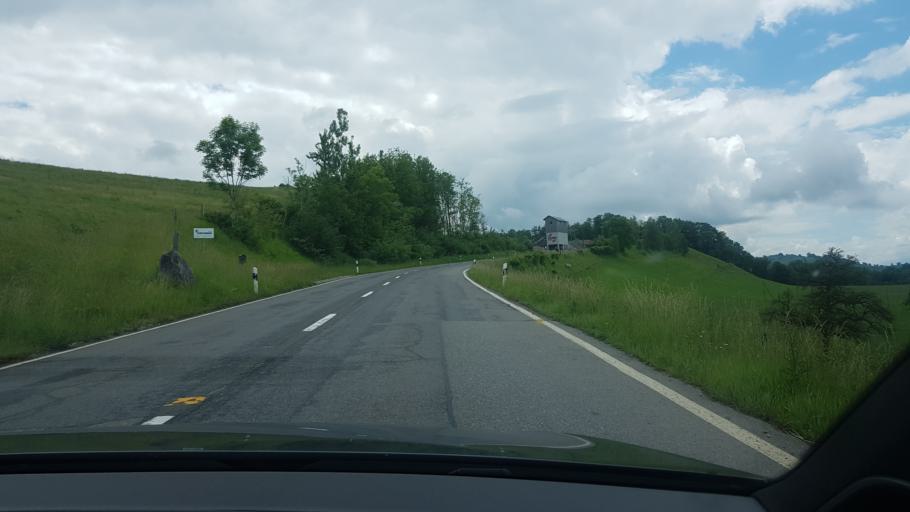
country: CH
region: Zug
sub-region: Zug
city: Menzingen
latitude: 47.1934
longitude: 8.5712
